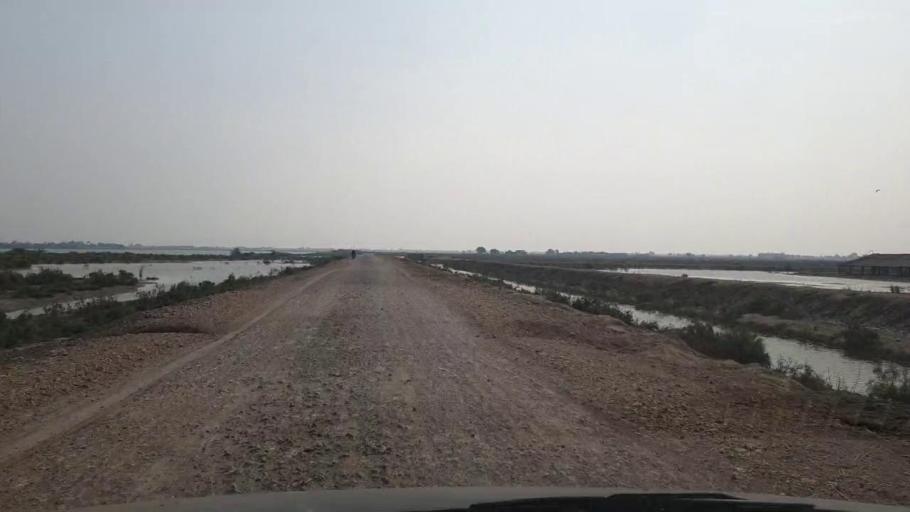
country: PK
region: Sindh
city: Tando Muhammad Khan
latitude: 25.0871
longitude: 68.3858
